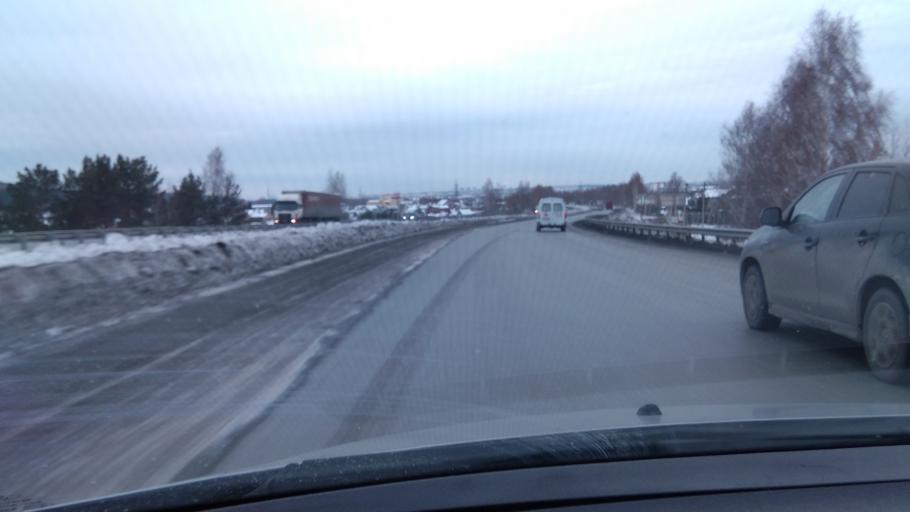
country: RU
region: Sverdlovsk
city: Aramil
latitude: 56.6970
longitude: 60.7507
